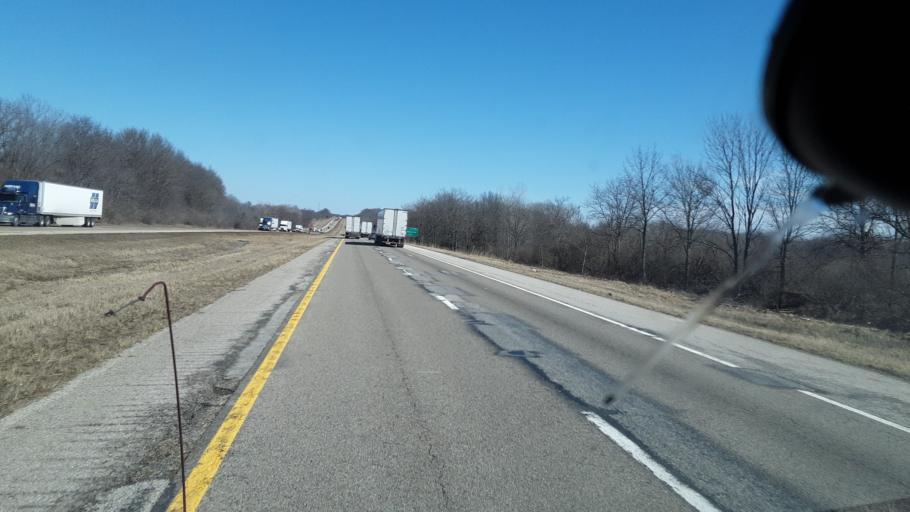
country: US
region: Illinois
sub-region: Clark County
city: Martinsville
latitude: 39.3507
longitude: -87.9080
